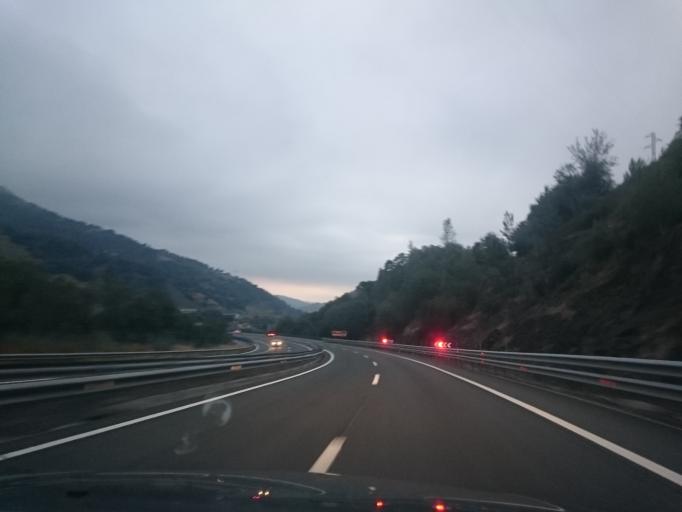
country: ES
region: Asturias
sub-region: Province of Asturias
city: Pola de Lena
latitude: 43.1008
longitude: -5.8186
